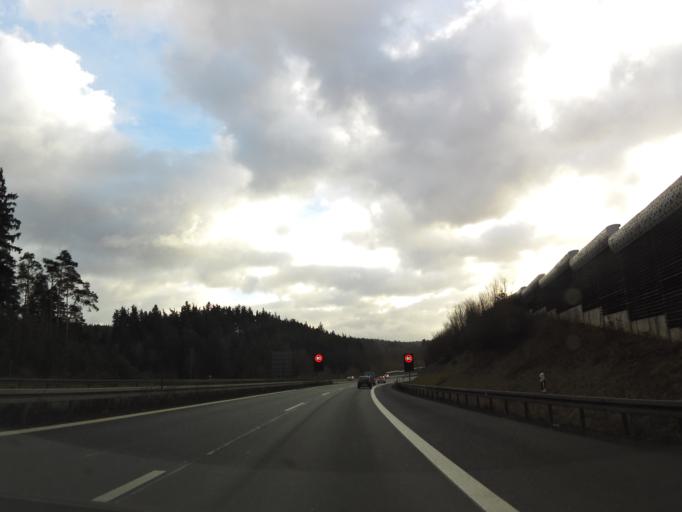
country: DE
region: Bavaria
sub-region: Upper Franconia
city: Selb
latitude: 50.1621
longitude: 12.1081
